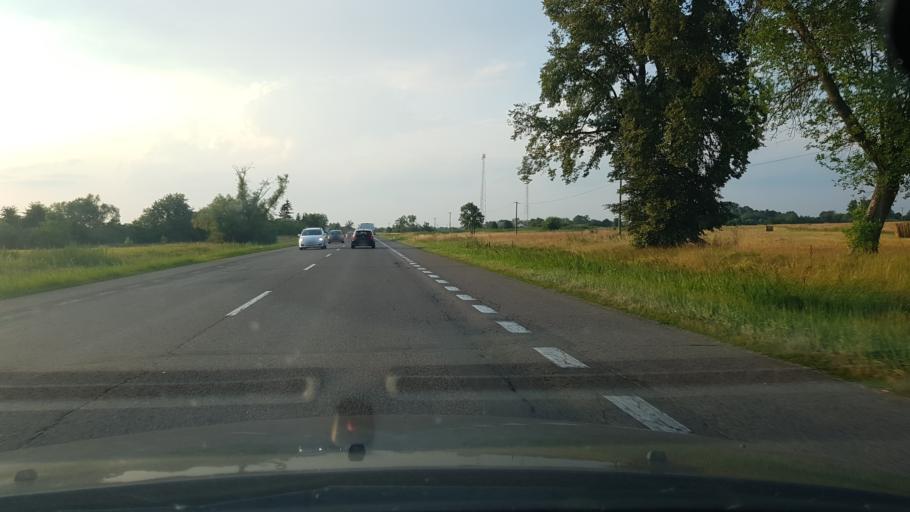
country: PL
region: Masovian Voivodeship
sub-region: Powiat plonski
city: Baboszewo
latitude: 52.7139
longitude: 20.3281
